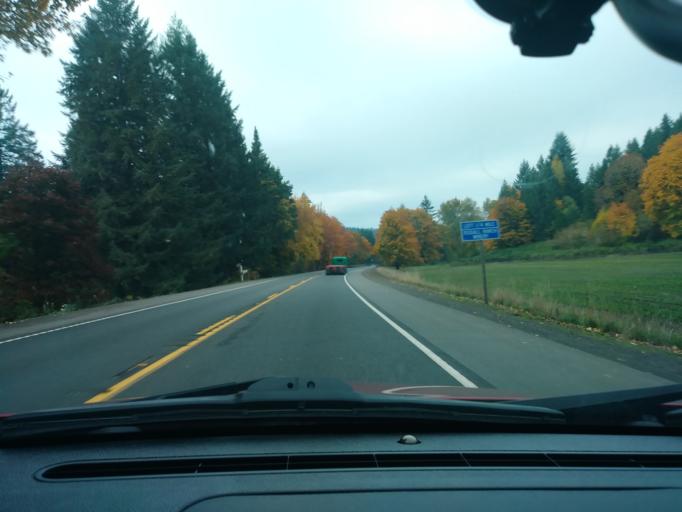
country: US
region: Oregon
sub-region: Washington County
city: Banks
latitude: 45.6100
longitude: -123.2397
